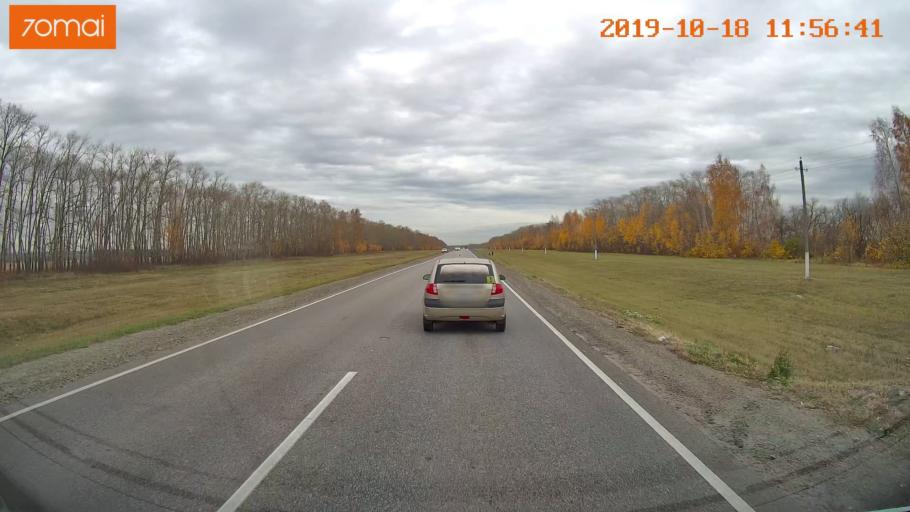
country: RU
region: Rjazan
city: Mikhaylov
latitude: 54.2658
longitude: 39.1236
